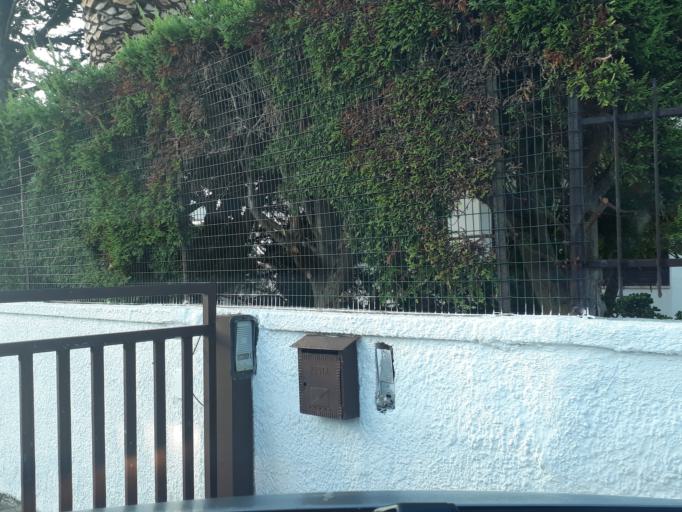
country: IT
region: Apulia
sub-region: Provincia di Brindisi
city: Carovigno
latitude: 40.7556
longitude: 17.6922
